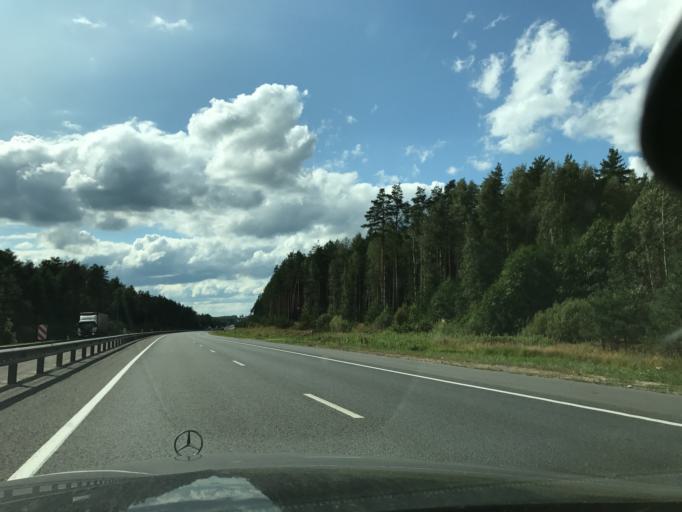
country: RU
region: Vladimir
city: Sudogda
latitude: 56.1127
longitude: 40.8370
